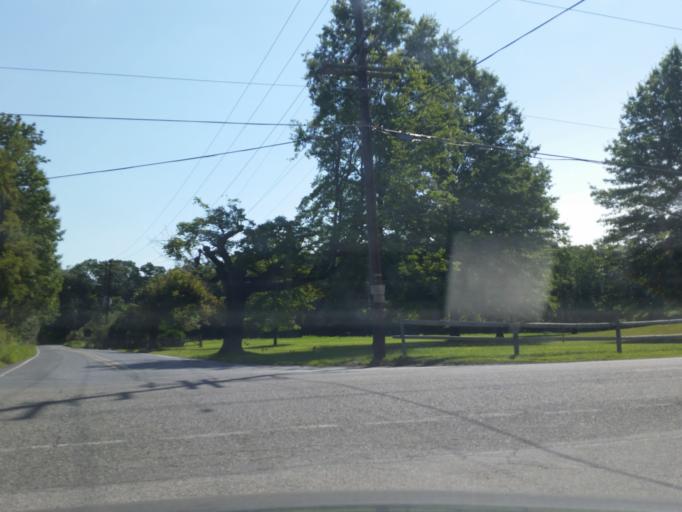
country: US
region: Pennsylvania
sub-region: Lebanon County
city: Jonestown
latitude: 40.4642
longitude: -76.5143
